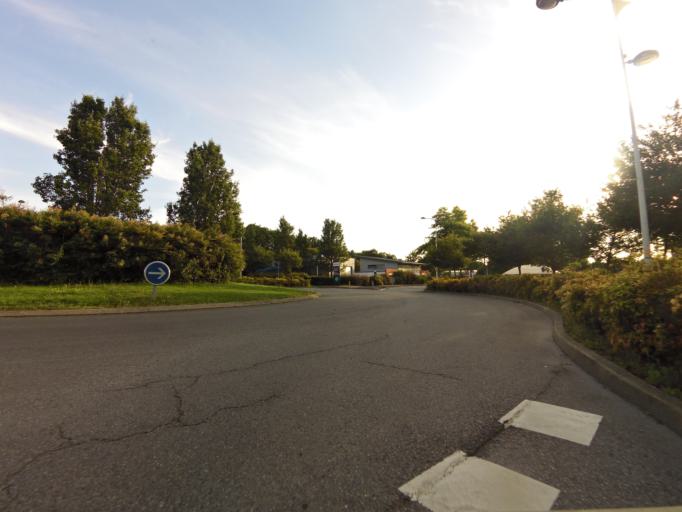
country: FR
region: Brittany
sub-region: Departement du Morbihan
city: Ploeren
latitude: 47.6587
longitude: -2.8691
